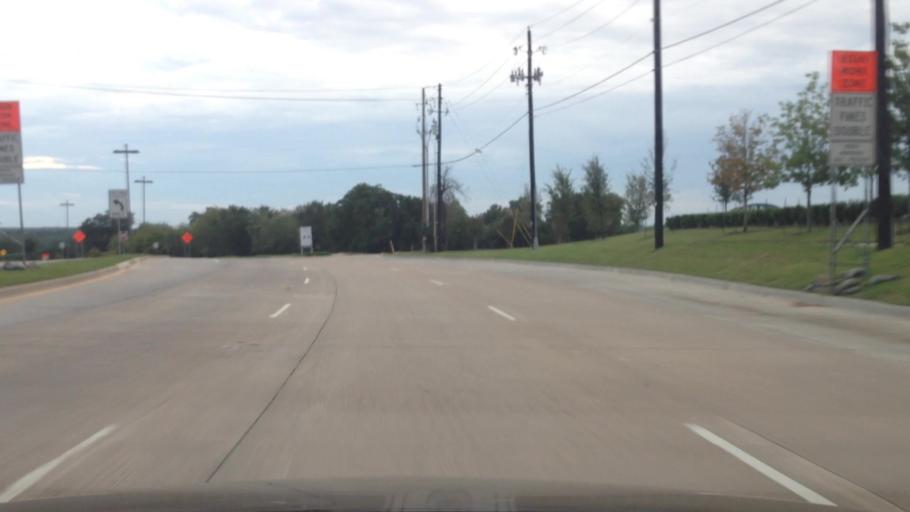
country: US
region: Texas
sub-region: Dallas County
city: Coppell
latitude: 32.9909
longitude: -97.0458
